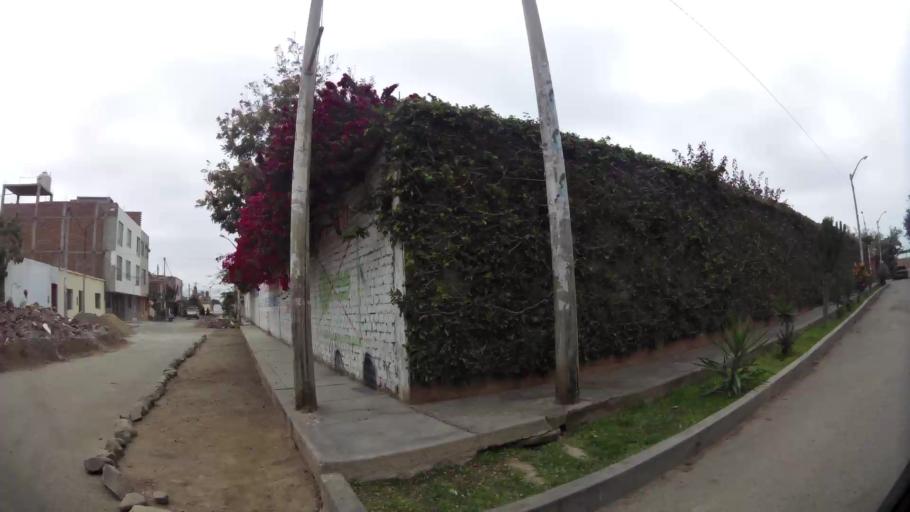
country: PE
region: La Libertad
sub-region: Provincia de Trujillo
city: La Esperanza
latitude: -8.0968
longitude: -79.0642
